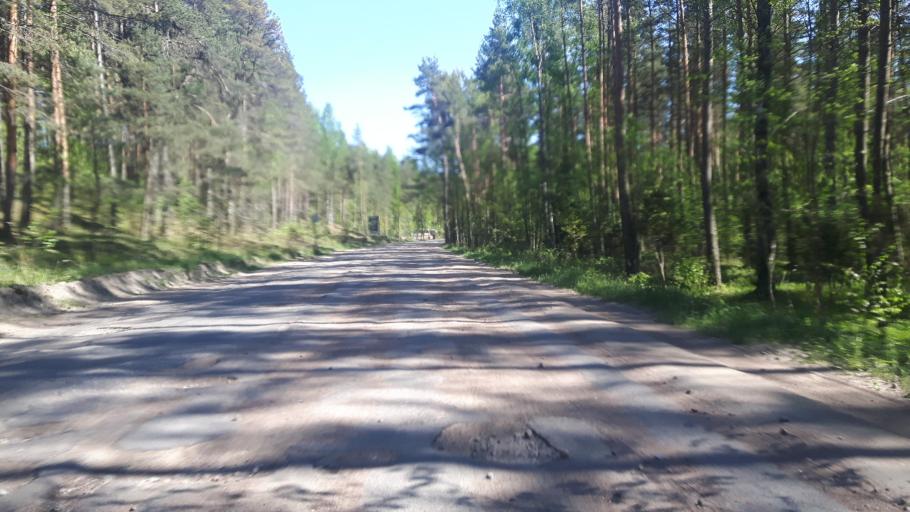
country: RU
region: Leningrad
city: Glebychevo
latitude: 60.2426
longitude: 28.9988
